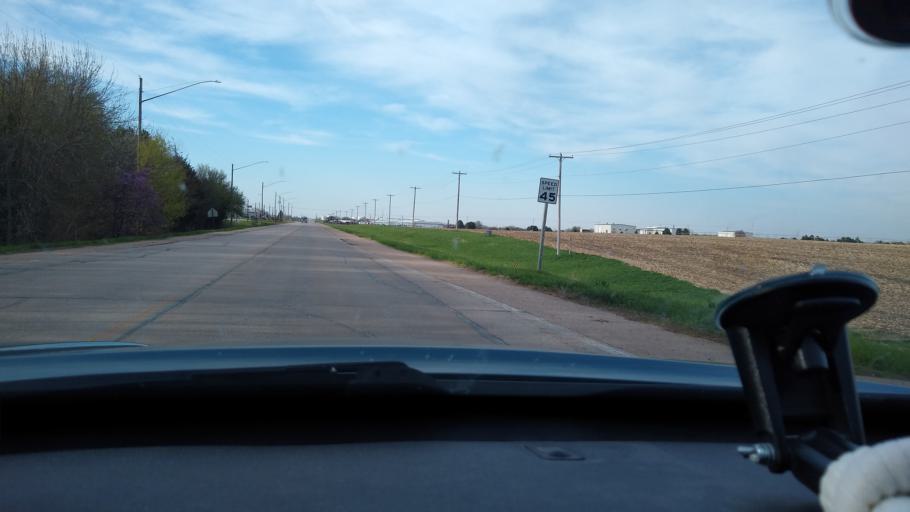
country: US
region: Nebraska
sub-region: Fillmore County
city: Geneva
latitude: 40.5339
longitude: -97.5958
